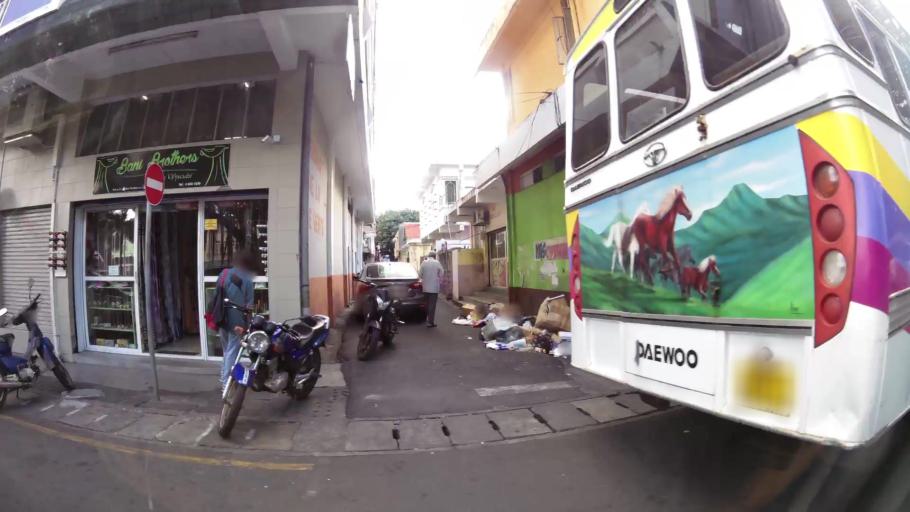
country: MU
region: Port Louis
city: Port Louis
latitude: -20.1592
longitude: 57.5120
